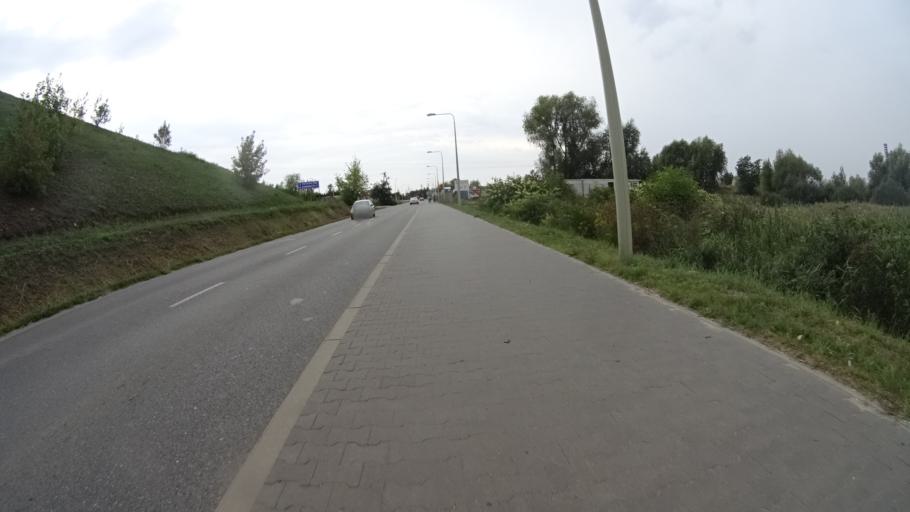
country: PL
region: Masovian Voivodeship
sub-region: Powiat pruszkowski
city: Pruszkow
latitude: 52.1775
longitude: 20.7726
